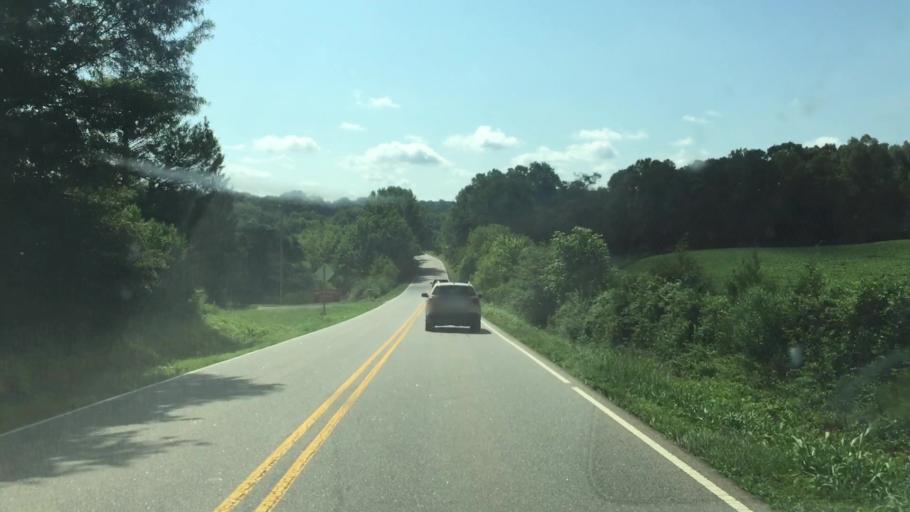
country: US
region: North Carolina
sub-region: Anson County
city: Burnsville
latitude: 35.0936
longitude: -80.3023
